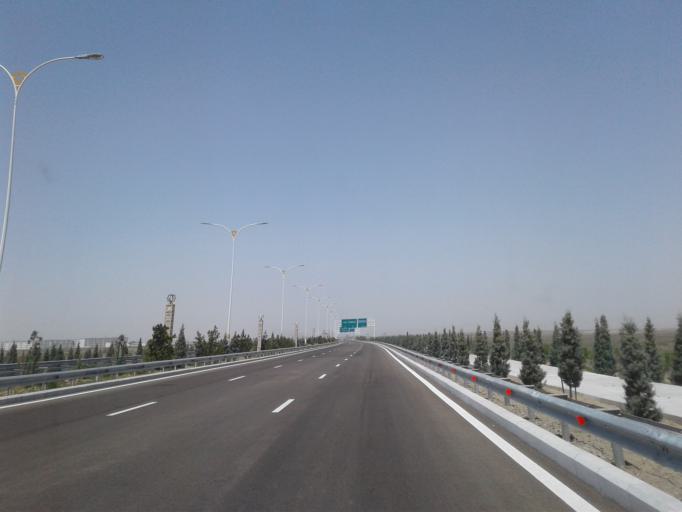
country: TM
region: Balkan
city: Turkmenbasy
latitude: 39.9696
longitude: 52.8663
